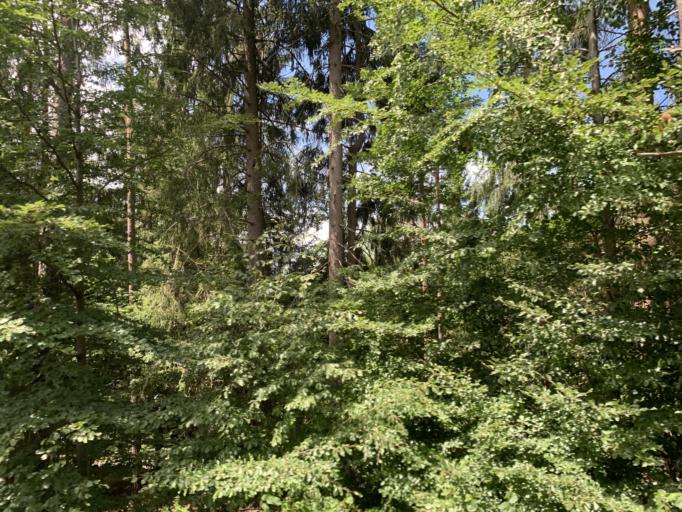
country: IT
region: Trentino-Alto Adige
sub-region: Bolzano
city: Soprabolzano
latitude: 46.5267
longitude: 11.4217
